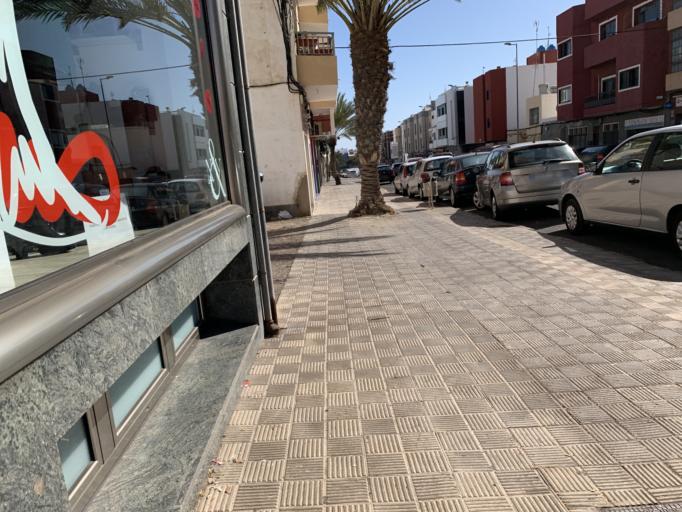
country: ES
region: Canary Islands
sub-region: Provincia de Las Palmas
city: Puerto del Rosario
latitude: 28.5008
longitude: -13.8677
